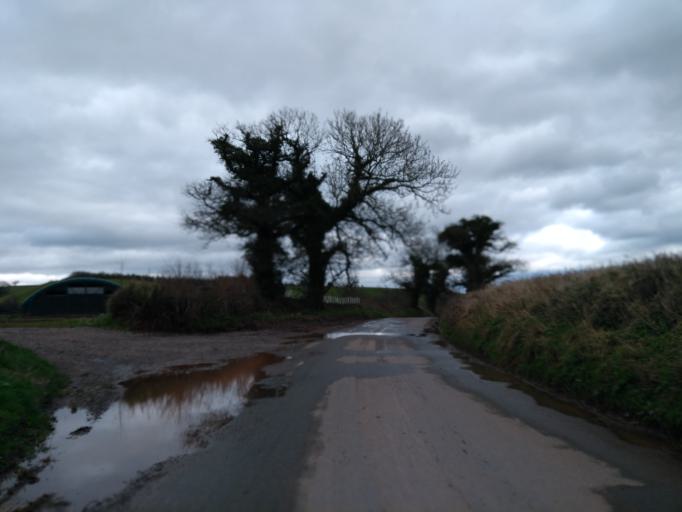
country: GB
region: England
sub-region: Devon
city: Crediton
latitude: 50.7868
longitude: -3.6122
